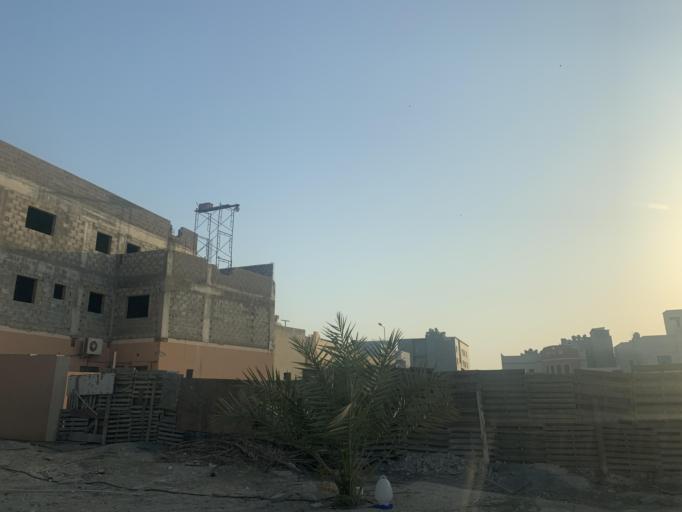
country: BH
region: Manama
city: Jidd Hafs
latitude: 26.2133
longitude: 50.5250
